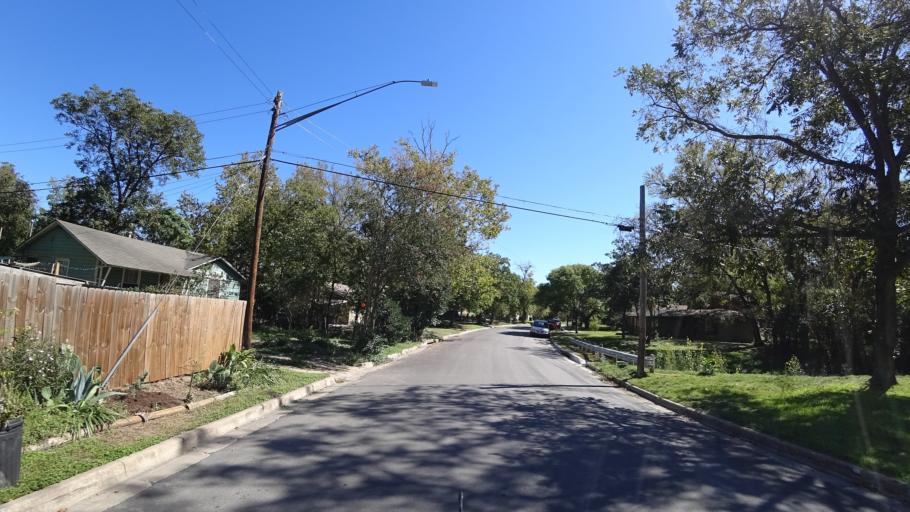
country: US
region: Texas
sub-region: Travis County
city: Austin
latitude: 30.2878
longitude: -97.7088
